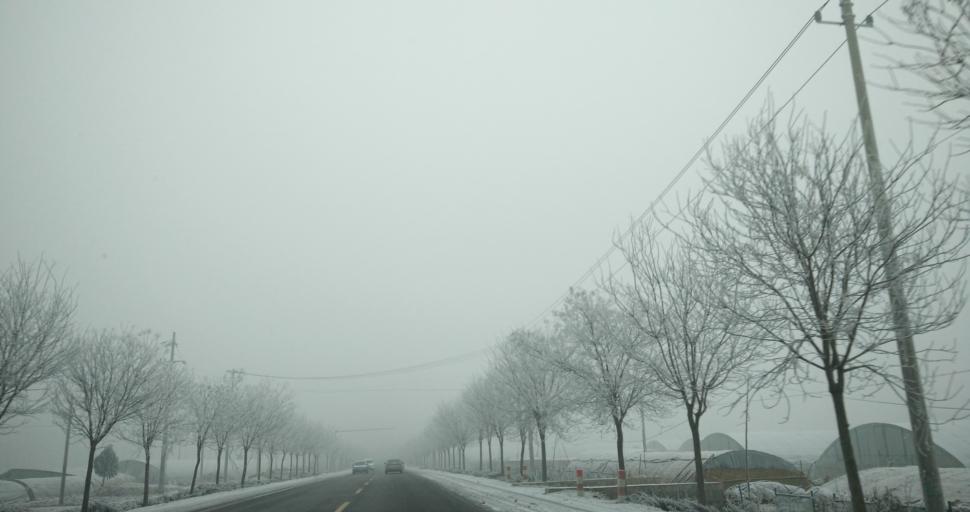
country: CN
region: Beijing
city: Yinghai
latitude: 39.7044
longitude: 116.4247
